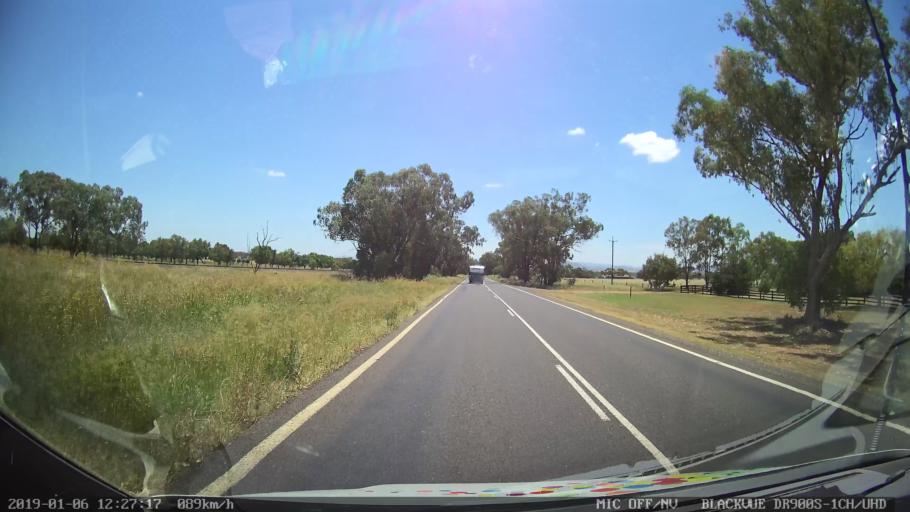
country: AU
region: New South Wales
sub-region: Tamworth Municipality
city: Phillip
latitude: -31.2084
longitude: 150.8268
